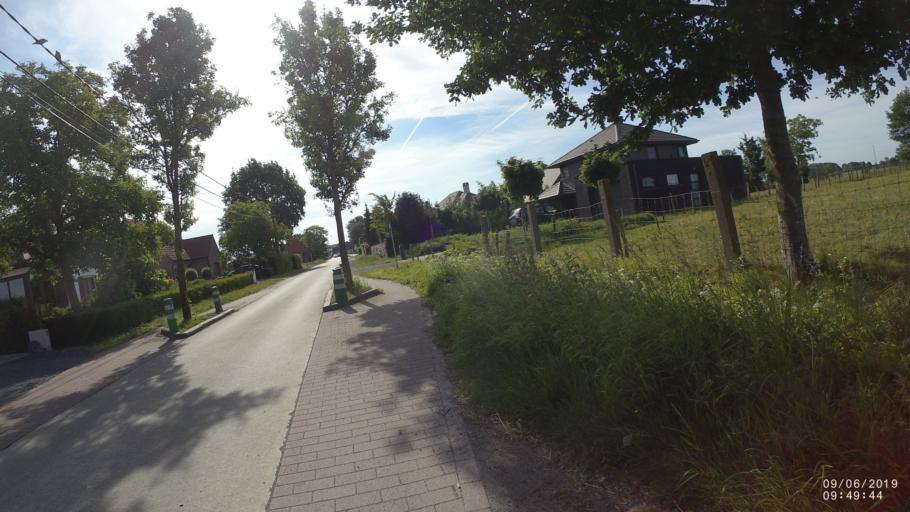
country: BE
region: Flanders
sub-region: Provincie Oost-Vlaanderen
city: Maldegem
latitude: 51.1918
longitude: 3.4906
